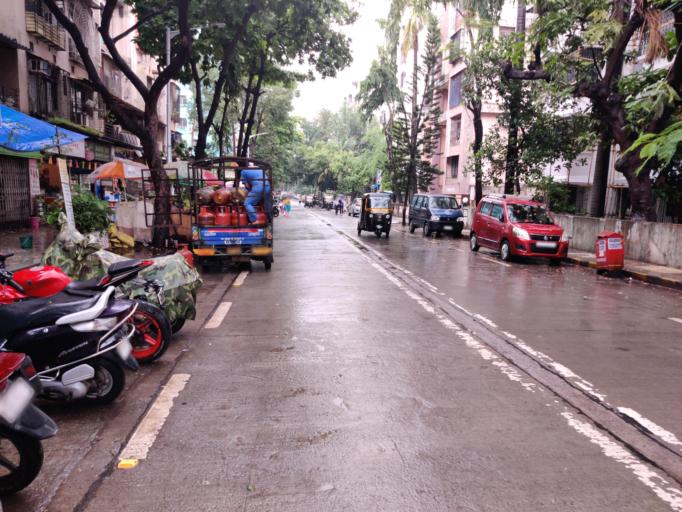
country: IN
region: Maharashtra
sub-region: Mumbai Suburban
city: Borivli
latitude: 19.2493
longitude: 72.8549
